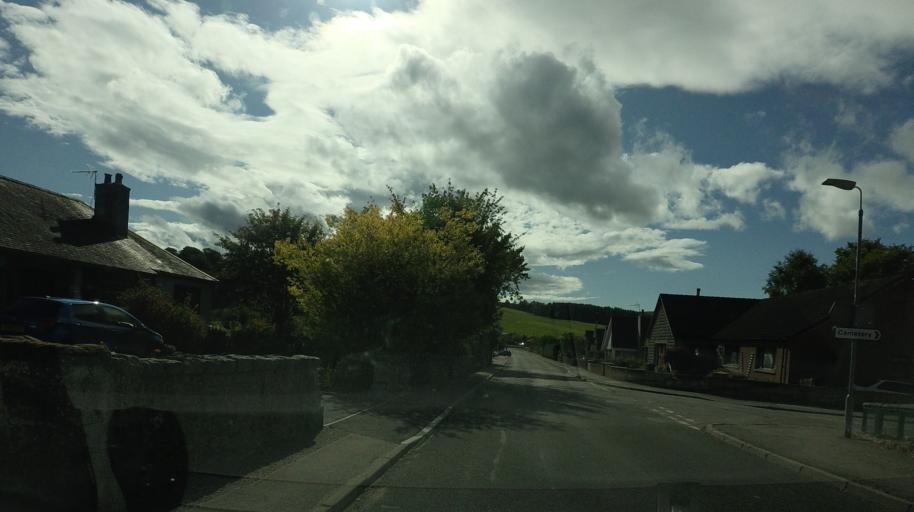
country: GB
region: Scotland
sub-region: Aberdeenshire
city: Torphins
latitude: 57.1286
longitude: -2.6885
